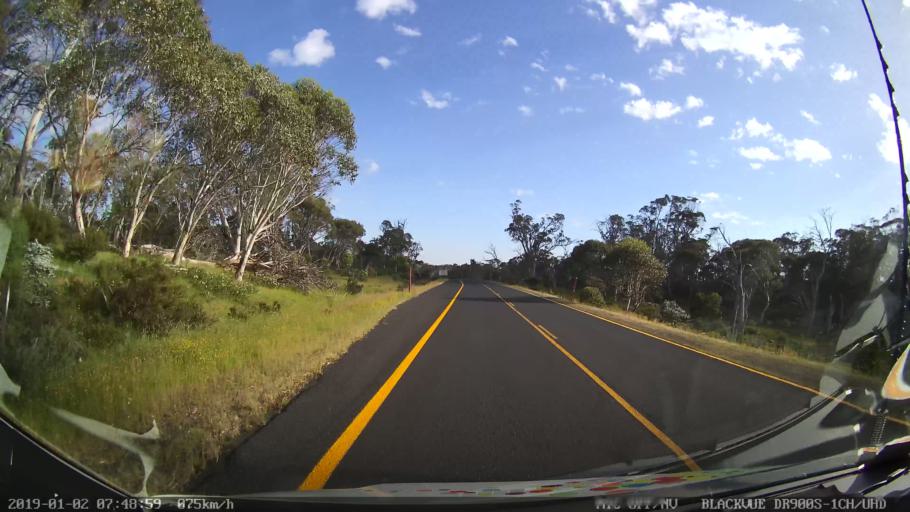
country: AU
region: New South Wales
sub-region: Tumut Shire
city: Tumut
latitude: -35.7468
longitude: 148.5208
